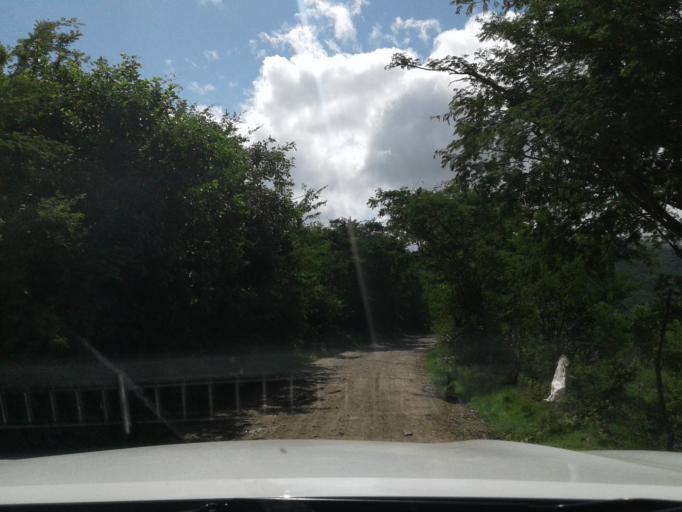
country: NI
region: Matagalpa
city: Ciudad Dario
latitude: 12.8465
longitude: -86.0828
